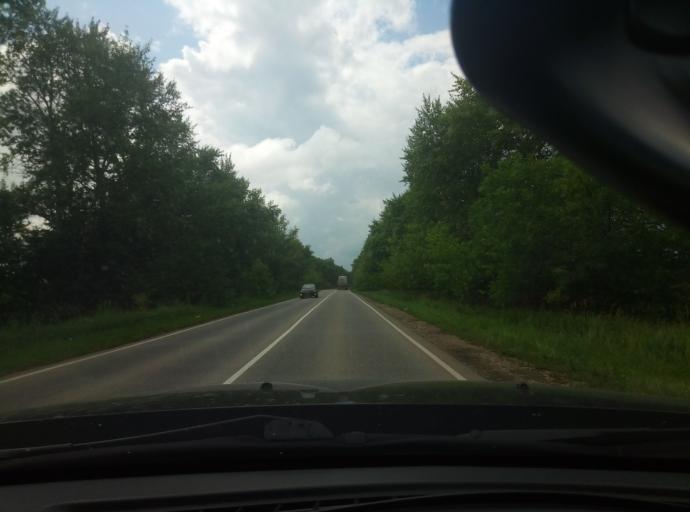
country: RU
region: Tula
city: Borodinskiy
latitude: 53.9898
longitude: 37.8024
